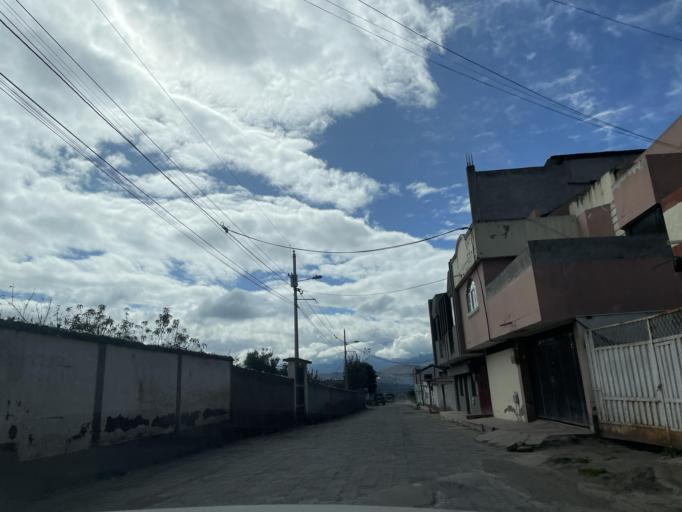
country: EC
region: Chimborazo
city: Guano
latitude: -1.6087
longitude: -78.6317
